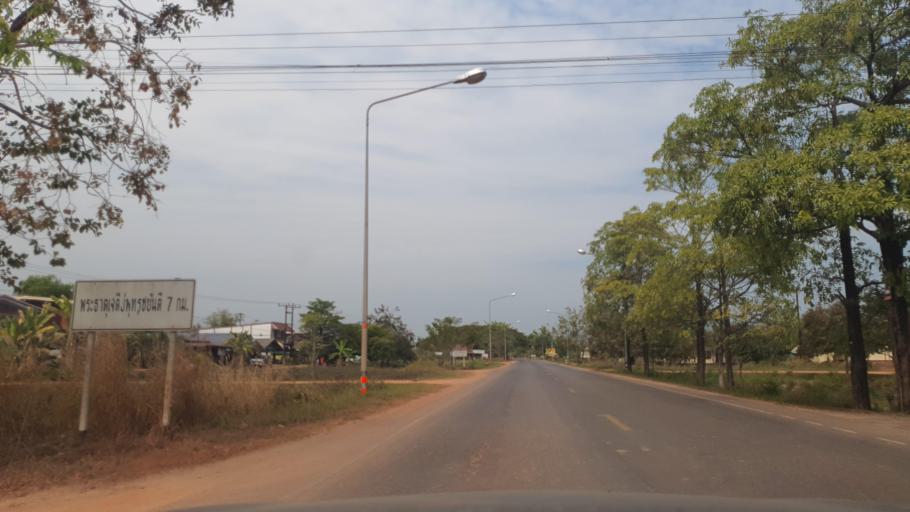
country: TH
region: Changwat Bueng Kan
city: Bung Khla
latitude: 18.1988
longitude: 104.0523
